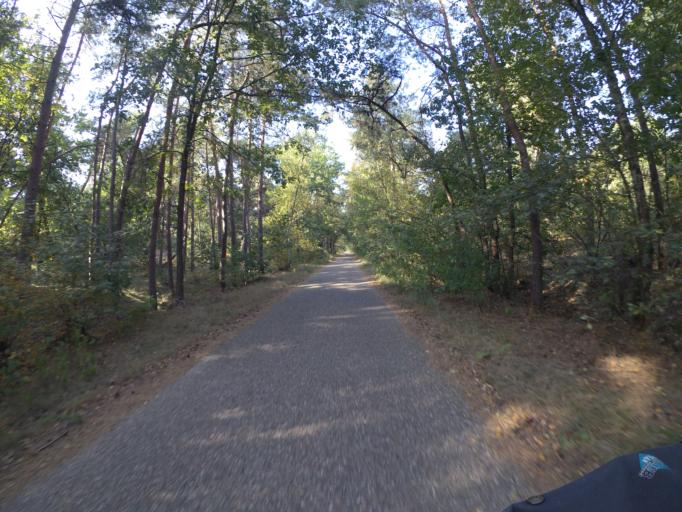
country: NL
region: North Brabant
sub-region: Gemeente Oirschot
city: Oirschot
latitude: 51.4701
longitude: 5.3325
